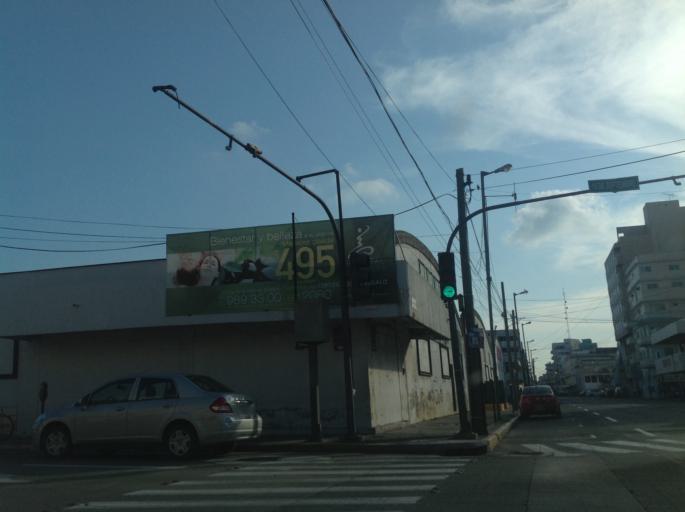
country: MX
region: Veracruz
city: Veracruz
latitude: 19.2011
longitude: -96.1346
